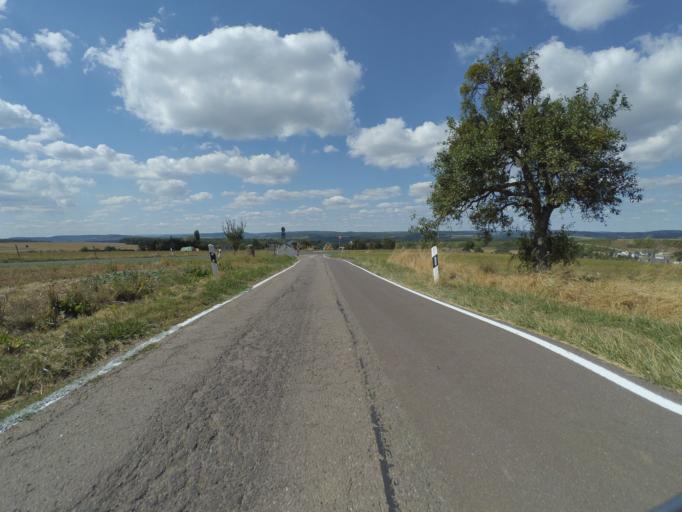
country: LU
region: Grevenmacher
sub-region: Canton de Grevenmacher
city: Wormeldange
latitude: 49.5836
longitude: 6.4205
